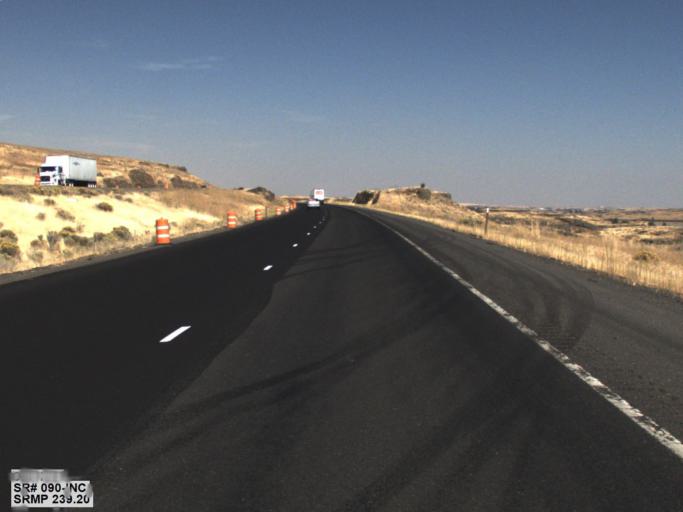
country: US
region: Washington
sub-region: Adams County
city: Ritzville
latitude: 47.2616
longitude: -118.0750
